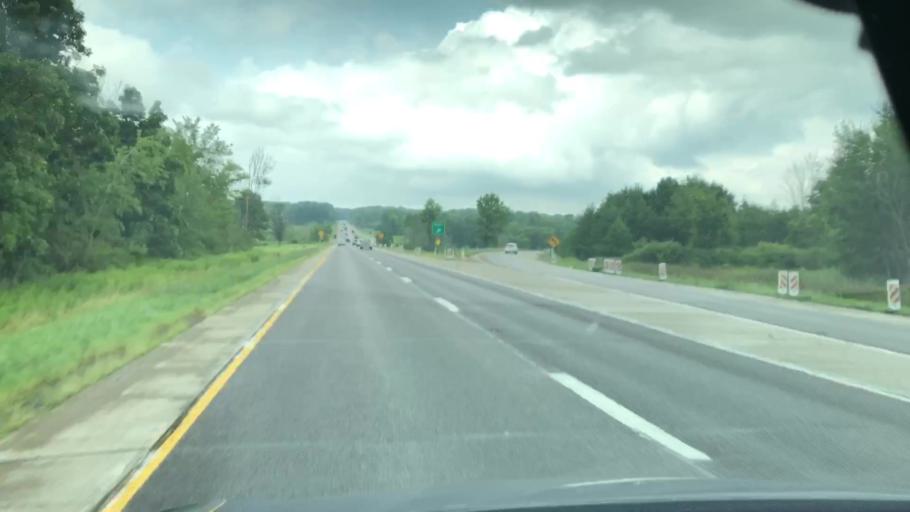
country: US
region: Pennsylvania
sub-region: Erie County
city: Fairview
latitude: 41.9940
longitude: -80.1679
